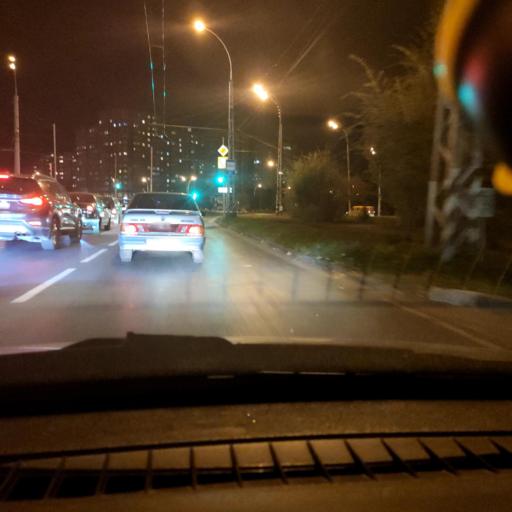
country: RU
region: Samara
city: Tol'yatti
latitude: 53.5182
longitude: 49.3112
